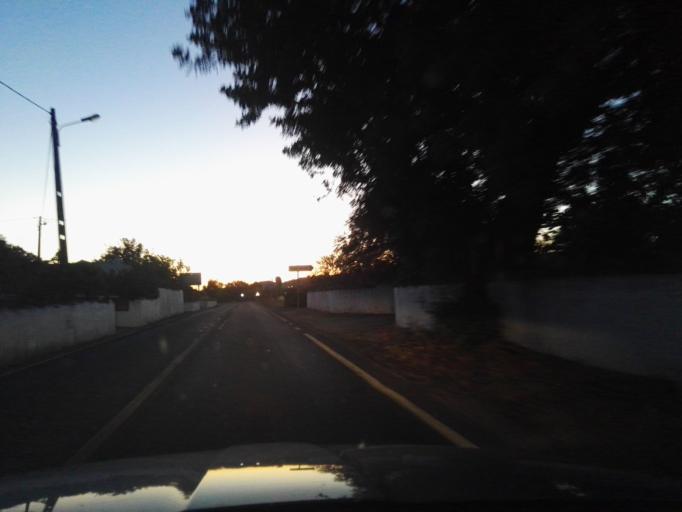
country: PT
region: Faro
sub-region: Faro
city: Santa Barbara de Nexe
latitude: 37.1507
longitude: -7.9413
